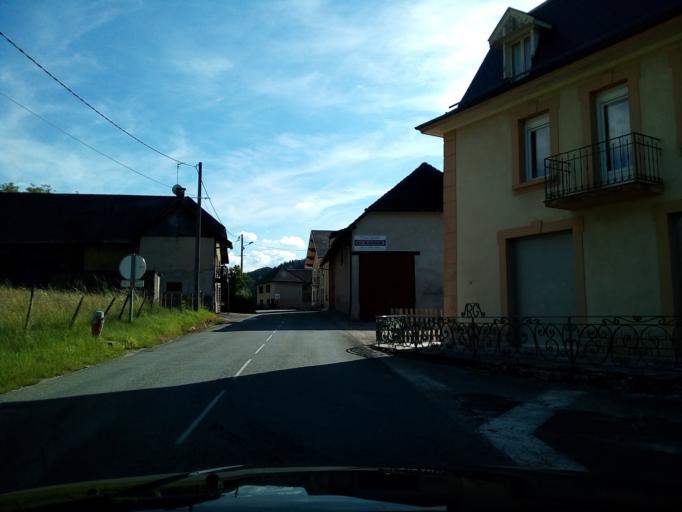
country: FR
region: Rhone-Alpes
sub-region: Departement de la Savoie
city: La Bridoire
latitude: 45.5082
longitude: 5.7693
